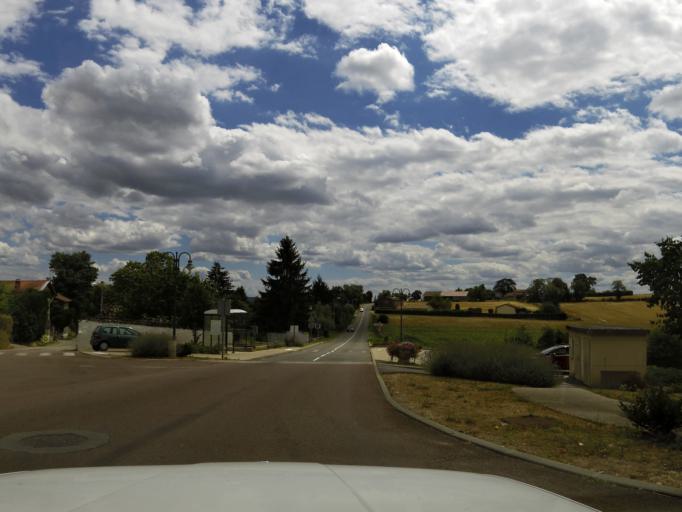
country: FR
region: Rhone-Alpes
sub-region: Departement de l'Ain
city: Saint-Jean-de-Niost
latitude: 45.8341
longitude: 5.2211
